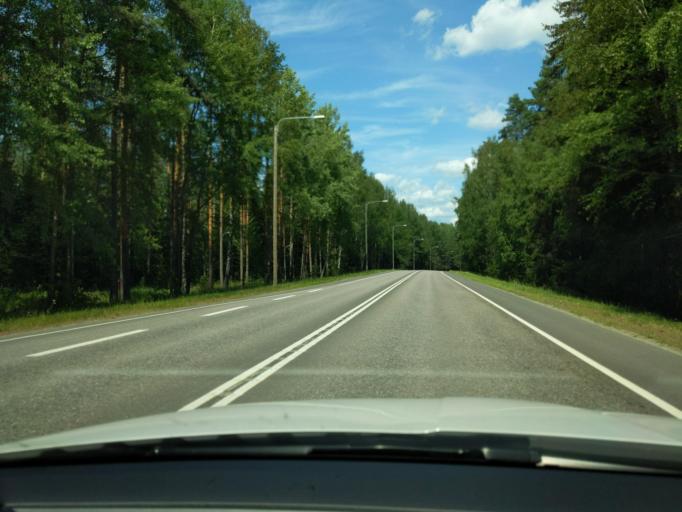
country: FI
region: Paijanne Tavastia
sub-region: Lahti
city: Heinola
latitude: 61.1783
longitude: 25.9933
